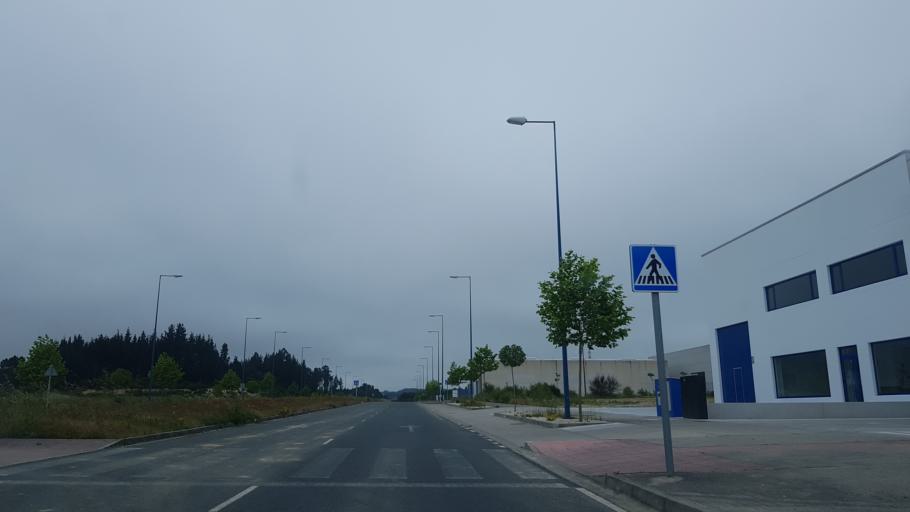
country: ES
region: Galicia
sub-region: Provincia de Lugo
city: Lugo
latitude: 43.0436
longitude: -7.5529
